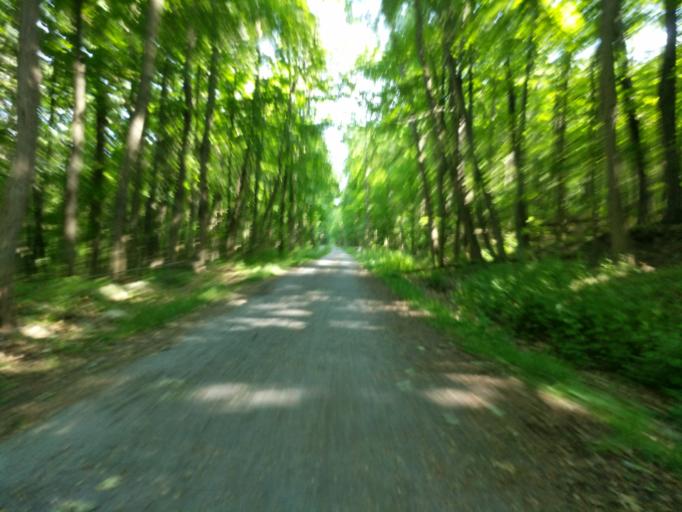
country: US
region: New York
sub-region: Tompkins County
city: Northwest Ithaca
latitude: 42.4808
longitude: -76.5359
